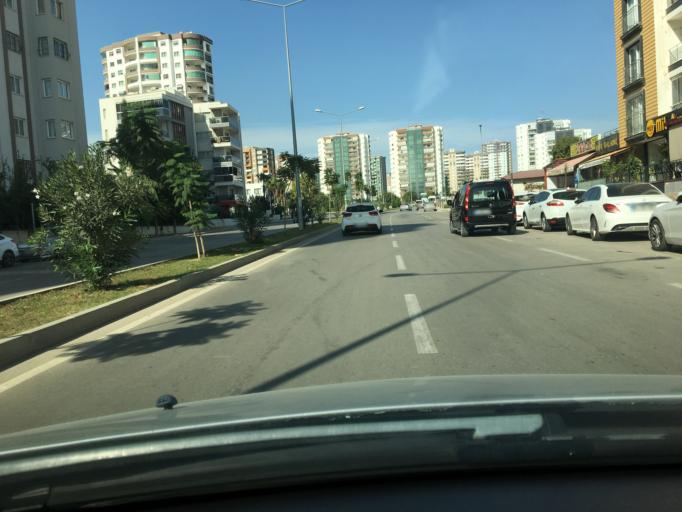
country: TR
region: Adana
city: Seyhan
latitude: 37.0207
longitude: 35.2582
